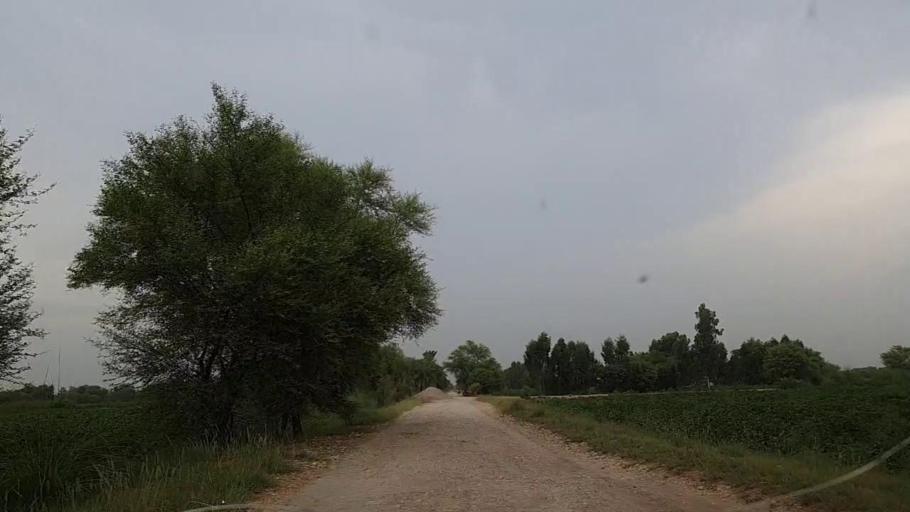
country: PK
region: Sindh
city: Khanpur
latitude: 27.8324
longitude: 69.6122
